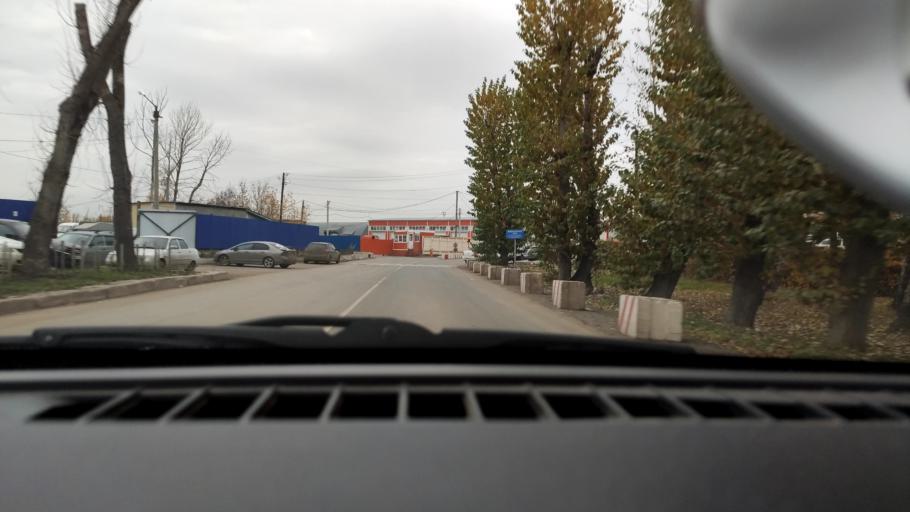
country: RU
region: Perm
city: Kondratovo
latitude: 58.0055
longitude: 56.1387
